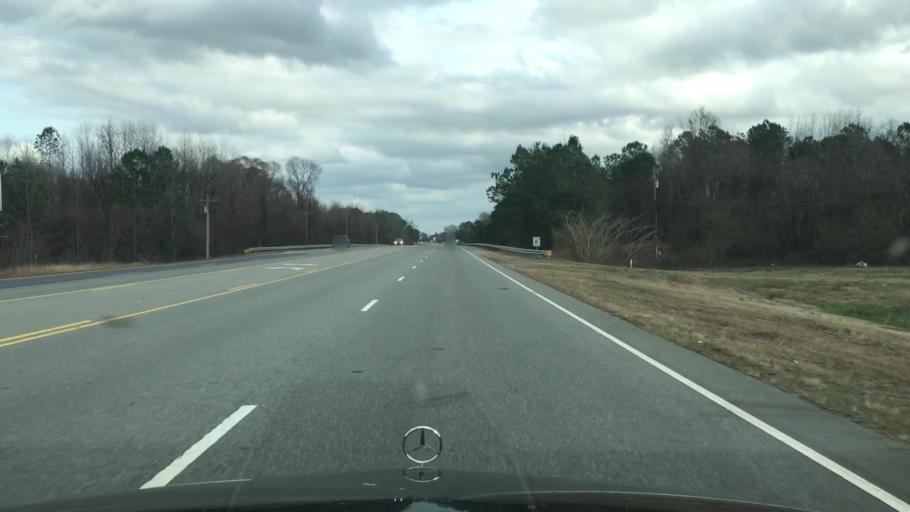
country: US
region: North Carolina
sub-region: Duplin County
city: Beulaville
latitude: 34.9284
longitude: -77.8050
